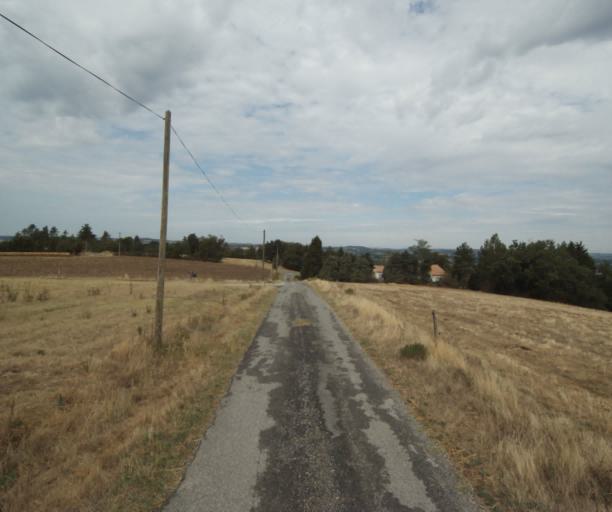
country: FR
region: Midi-Pyrenees
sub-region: Departement de la Haute-Garonne
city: Revel
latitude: 43.4399
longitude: 1.9867
